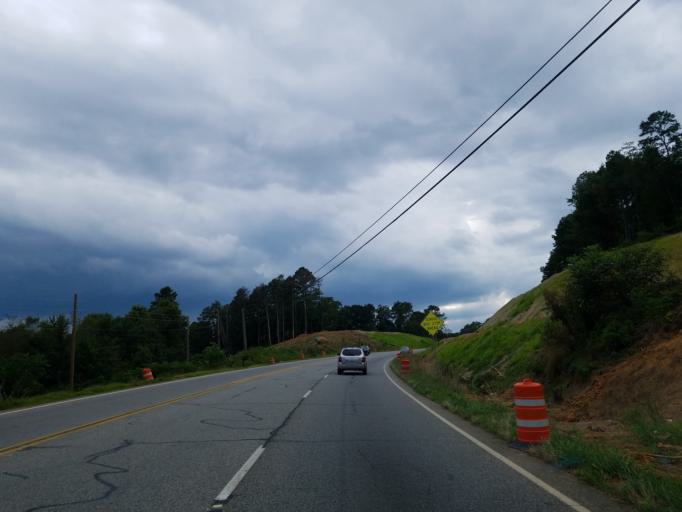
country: US
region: Georgia
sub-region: Bartow County
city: Adairsville
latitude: 34.3701
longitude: -84.9742
